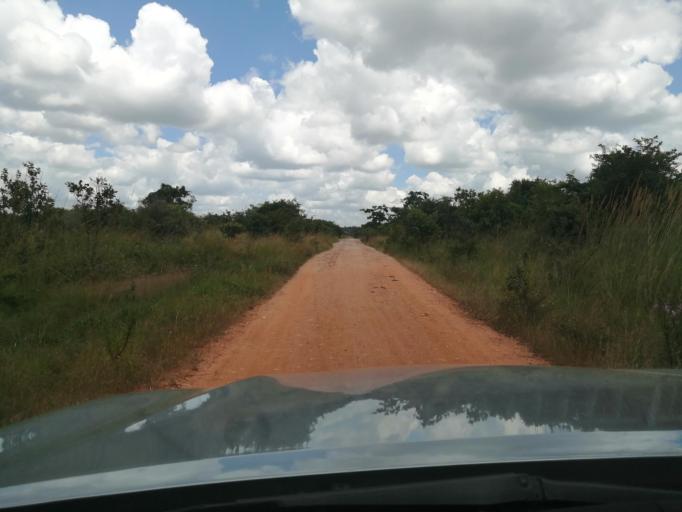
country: ZM
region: Lusaka
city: Lusaka
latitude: -15.1607
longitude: 27.9492
